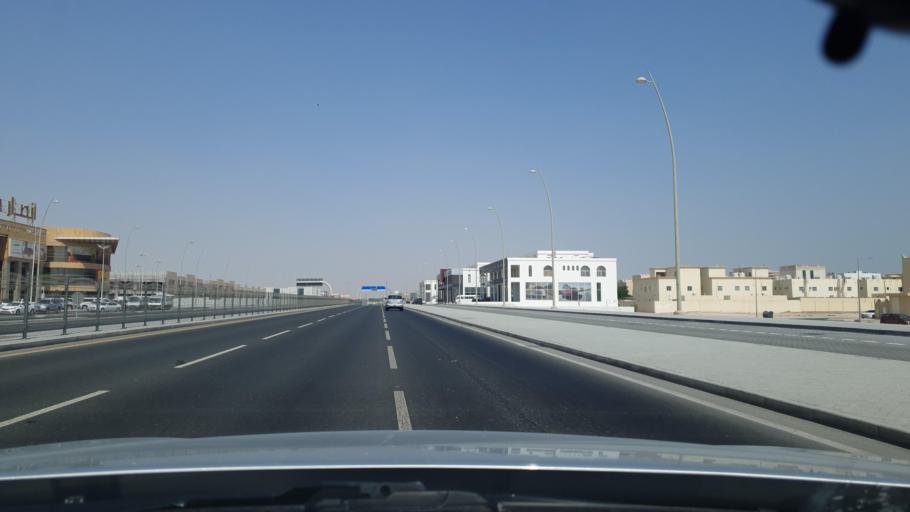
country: QA
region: Al Khawr
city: Al Khawr
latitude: 25.6649
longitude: 51.5011
